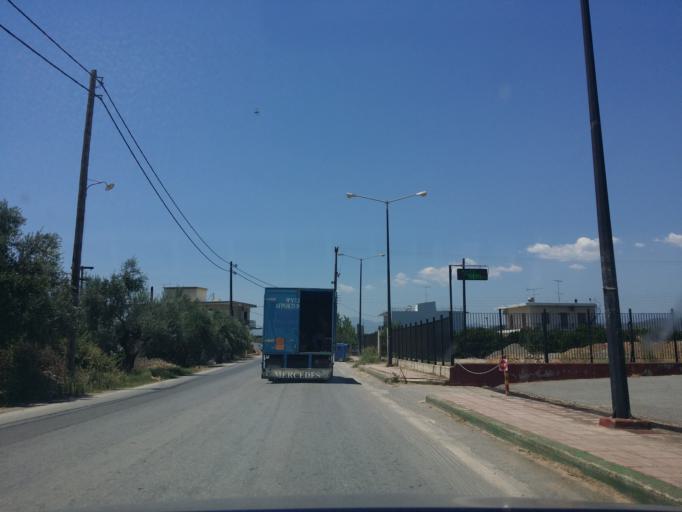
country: GR
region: Peloponnese
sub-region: Nomos Lakonias
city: Vlakhiotis
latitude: 36.8605
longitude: 22.7016
